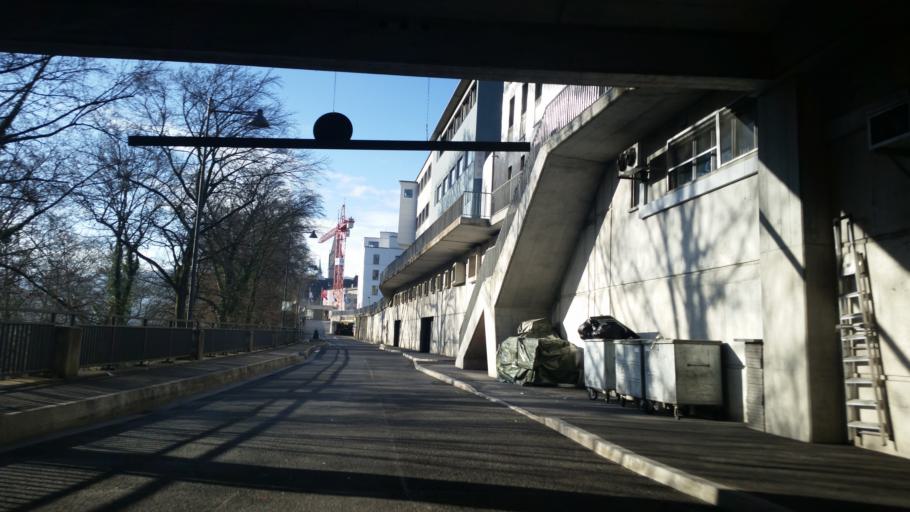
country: CH
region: Aargau
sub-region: Bezirk Baden
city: Baden
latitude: 47.4765
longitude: 8.3092
